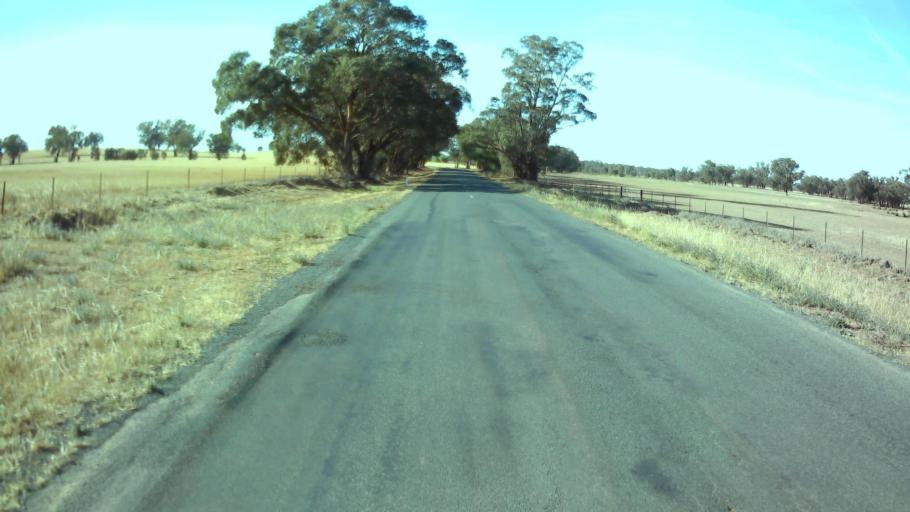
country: AU
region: New South Wales
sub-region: Weddin
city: Grenfell
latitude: -33.9733
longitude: 148.1409
